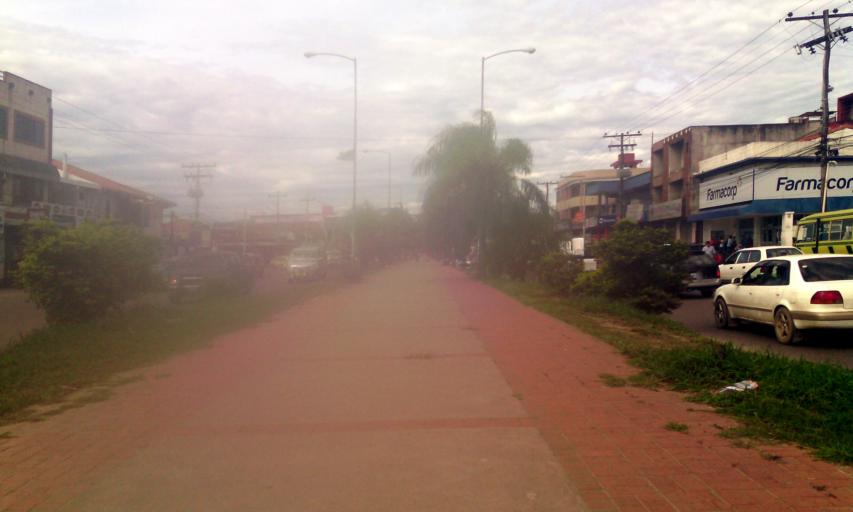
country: BO
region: Santa Cruz
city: Santa Cruz de la Sierra
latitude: -17.8272
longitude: -63.2257
